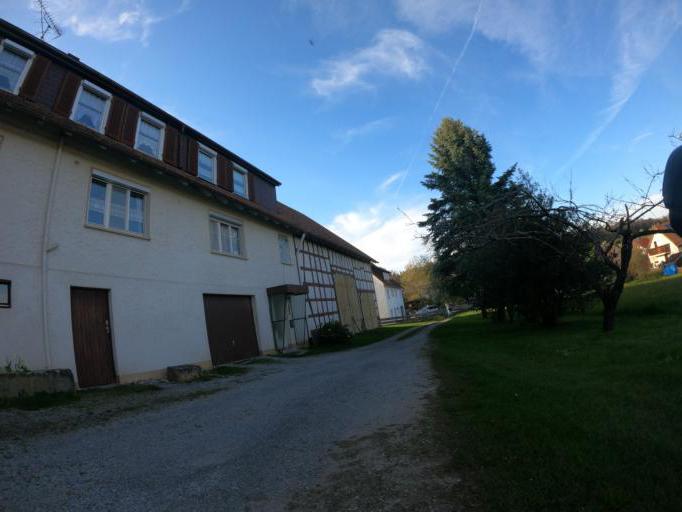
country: DE
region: Baden-Wuerttemberg
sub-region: Karlsruhe Region
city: Oberreichenbach
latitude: 48.7131
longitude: 8.6639
